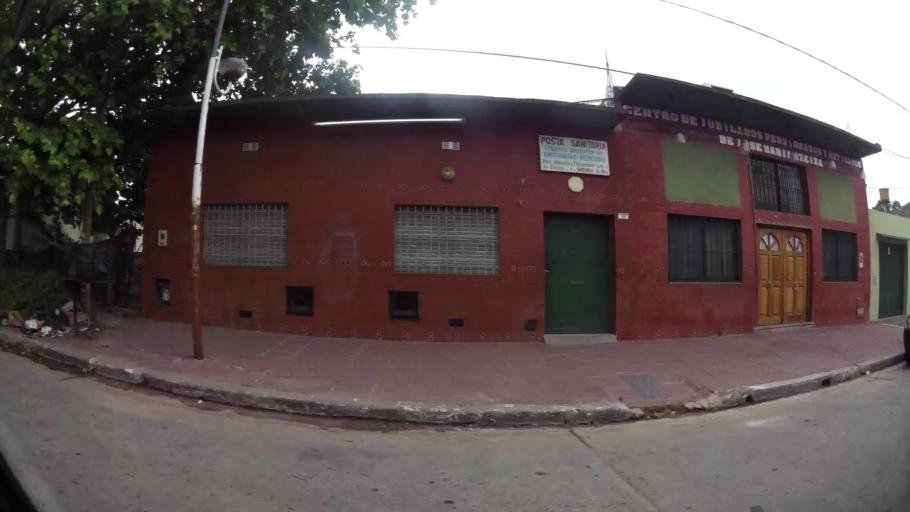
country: AR
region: Buenos Aires
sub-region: Partido de Ezeiza
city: Ezeiza
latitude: -34.8489
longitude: -58.5221
